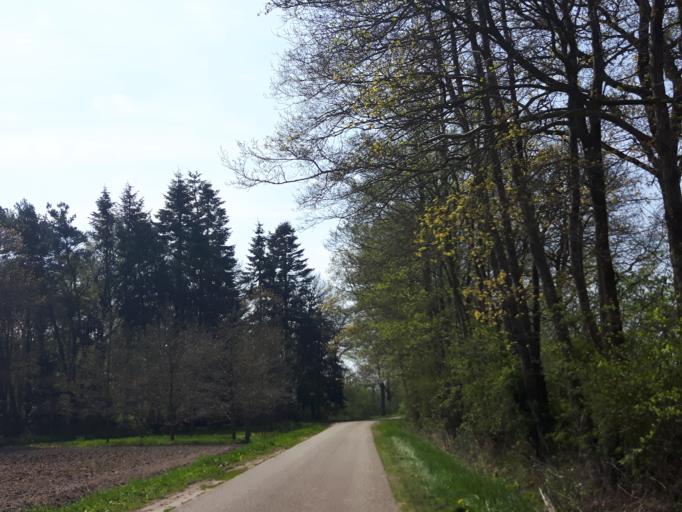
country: NL
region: Overijssel
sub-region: Gemeente Haaksbergen
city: Haaksbergen
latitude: 52.1334
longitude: 6.8276
